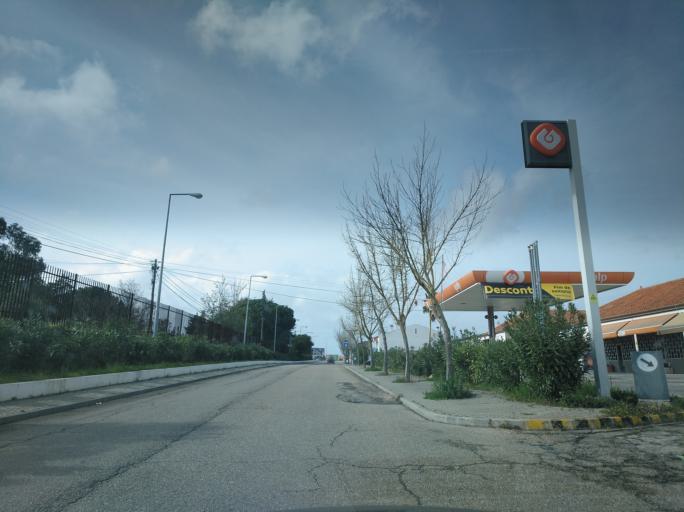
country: PT
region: Setubal
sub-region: Grandola
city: Grandola
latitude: 38.1705
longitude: -8.5566
